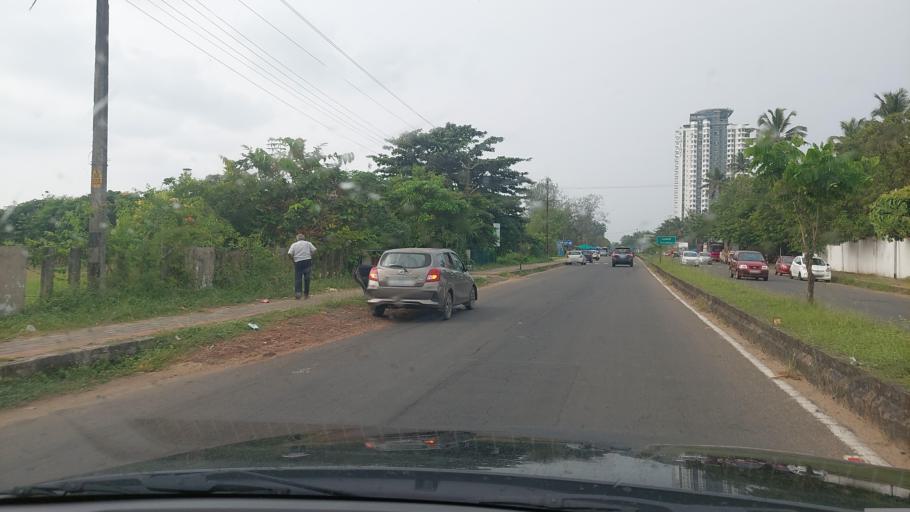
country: IN
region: Kerala
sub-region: Kozhikode
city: Kozhikode
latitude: 11.2880
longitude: 75.7596
